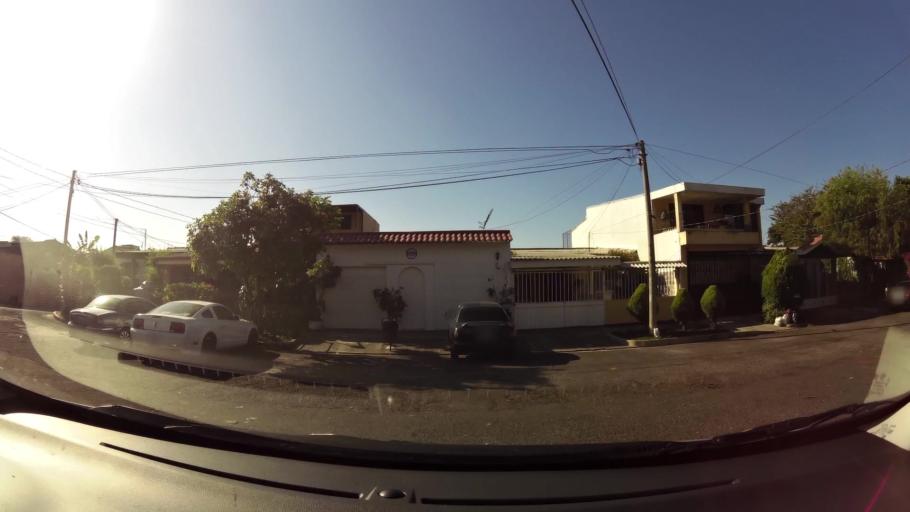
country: SV
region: La Libertad
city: Santa Tecla
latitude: 13.6912
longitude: -89.2928
